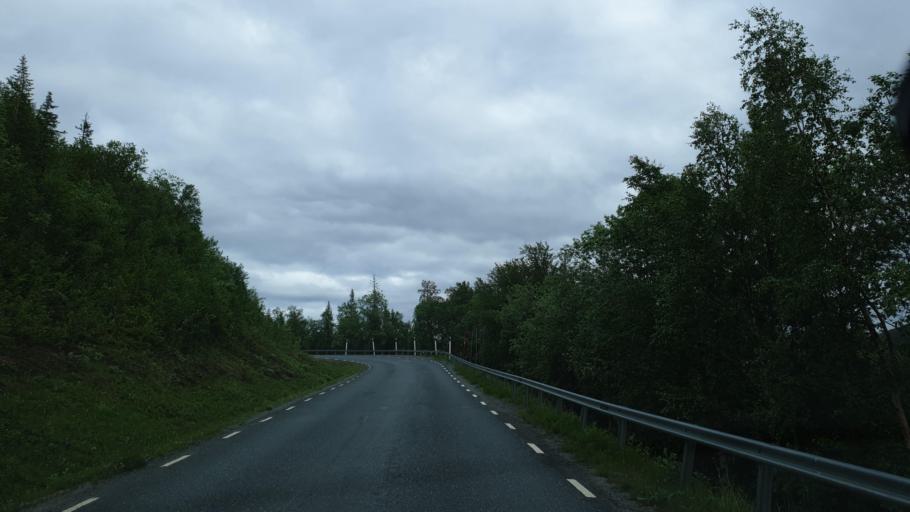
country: SE
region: Vaesterbotten
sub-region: Vilhelmina Kommun
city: Sjoberg
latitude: 65.2375
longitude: 15.4544
